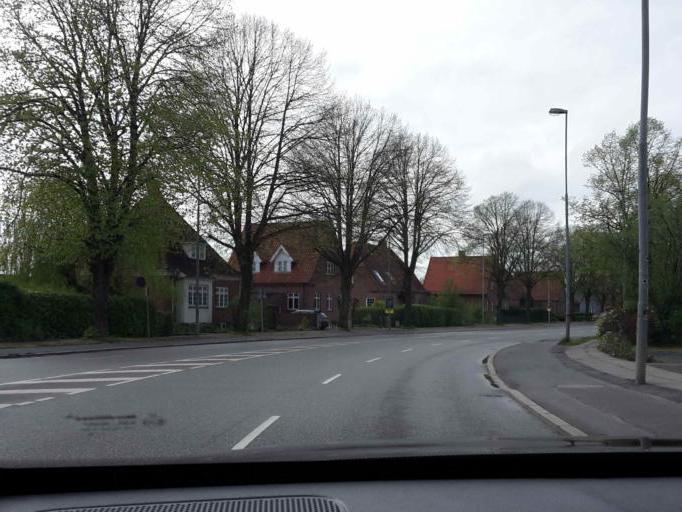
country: DK
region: South Denmark
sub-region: Odense Kommune
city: Odense
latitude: 55.3988
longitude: 10.3623
